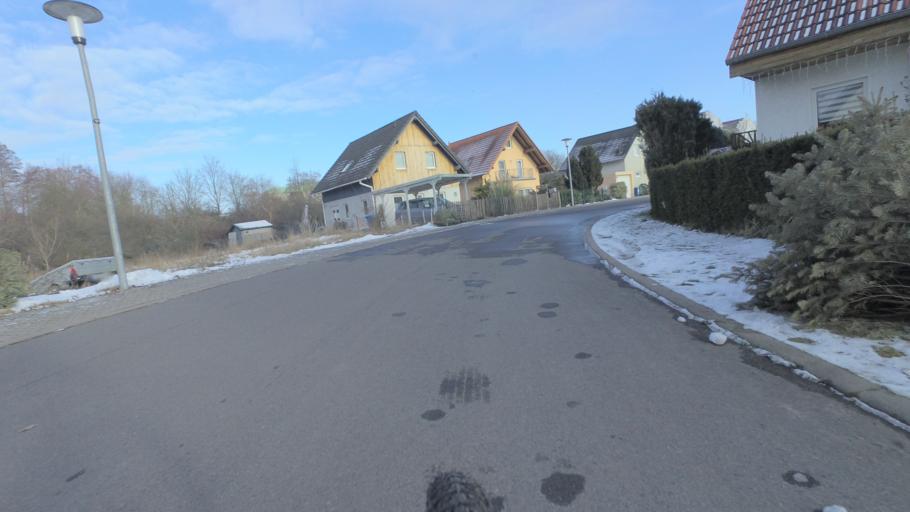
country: DE
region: Brandenburg
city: Zossen
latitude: 52.2404
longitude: 13.4181
